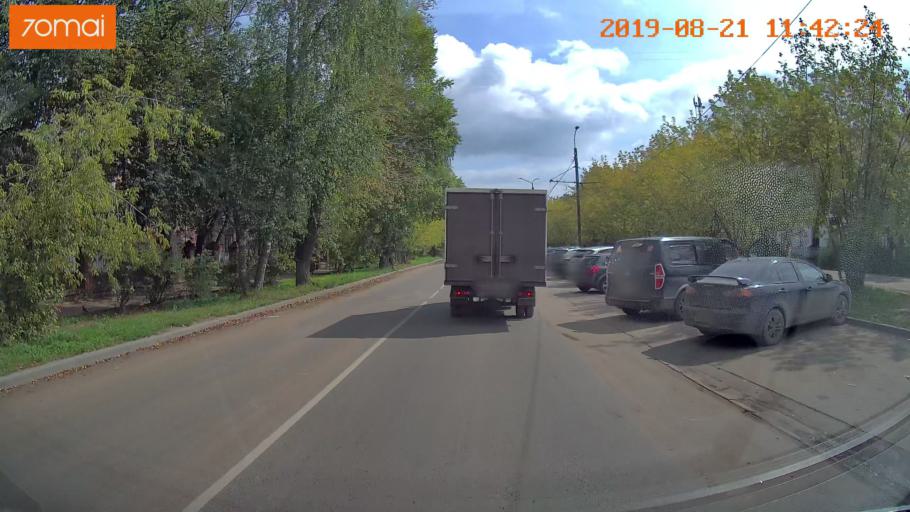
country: RU
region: Ivanovo
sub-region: Gorod Ivanovo
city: Ivanovo
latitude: 57.0022
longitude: 40.9489
